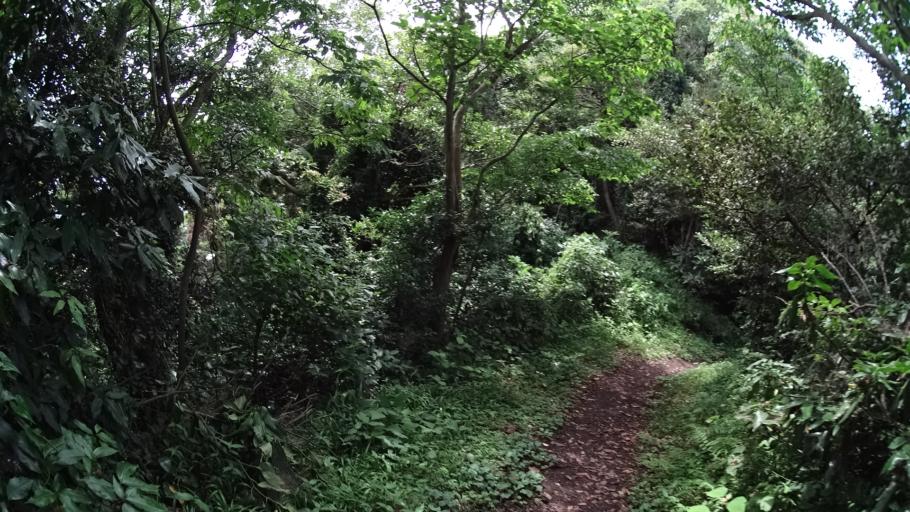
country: JP
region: Kanagawa
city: Yokosuka
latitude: 35.2168
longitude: 139.6676
